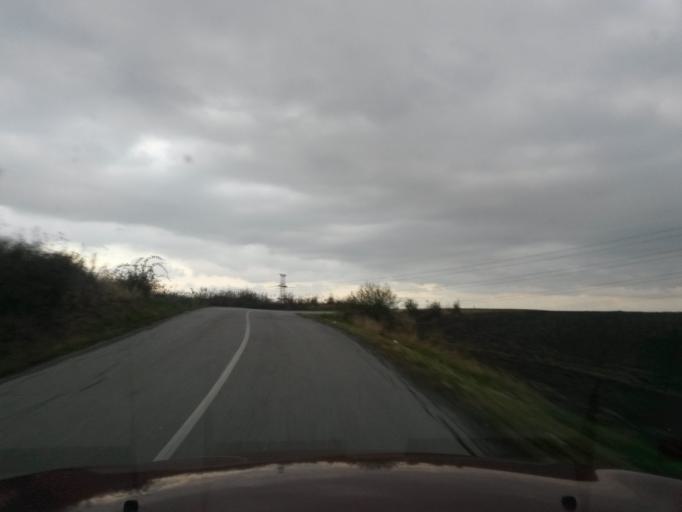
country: SK
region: Kosicky
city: Kosice
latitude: 48.8047
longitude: 21.2720
